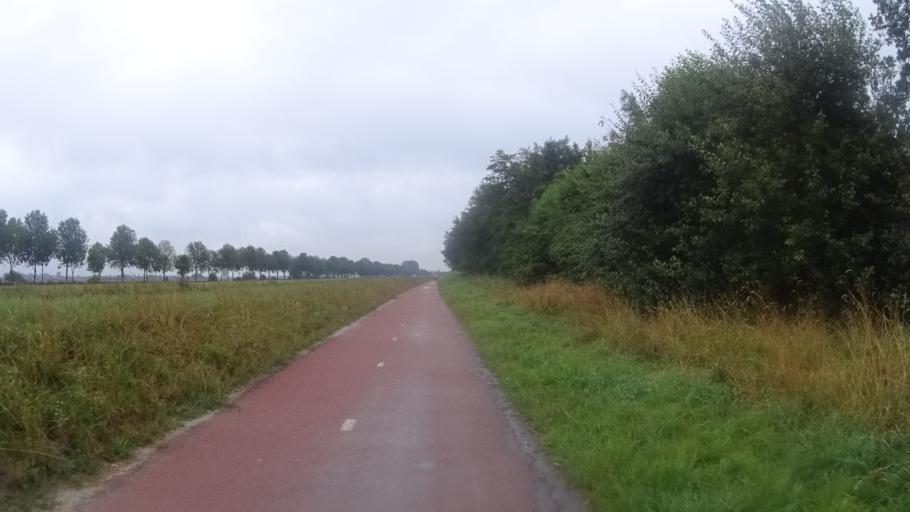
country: NL
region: Groningen
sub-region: Gemeente  Oldambt
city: Winschoten
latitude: 53.1609
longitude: 7.0273
